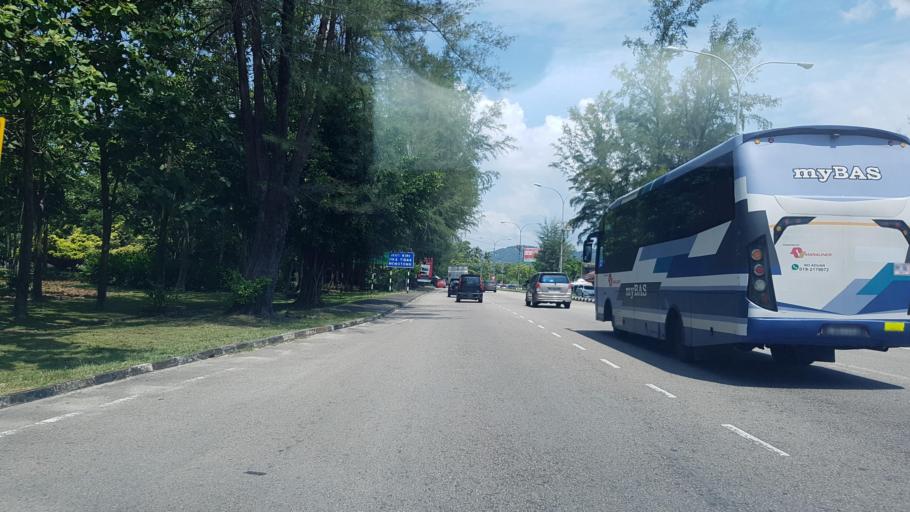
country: MY
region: Terengganu
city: Kuala Terengganu
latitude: 5.2840
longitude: 103.1690
